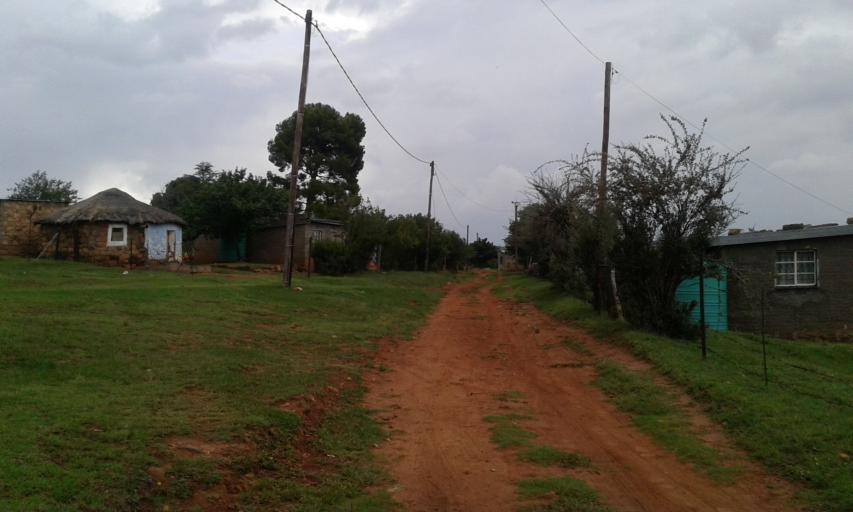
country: LS
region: Maseru
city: Maseru
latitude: -29.4249
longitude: 27.5741
